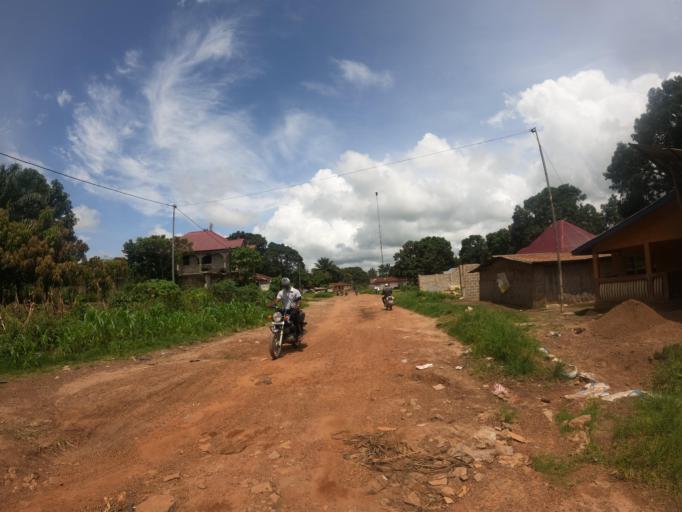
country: SL
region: Northern Province
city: Makeni
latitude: 8.8937
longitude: -12.0555
